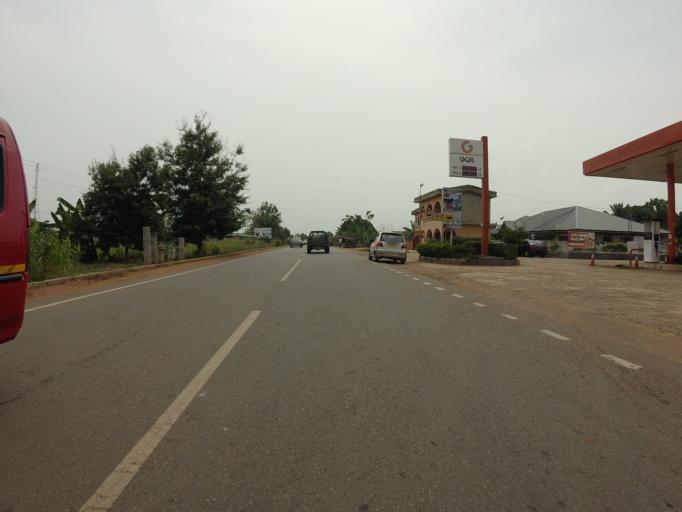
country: GH
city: Akropong
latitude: 6.0788
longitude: -0.0193
